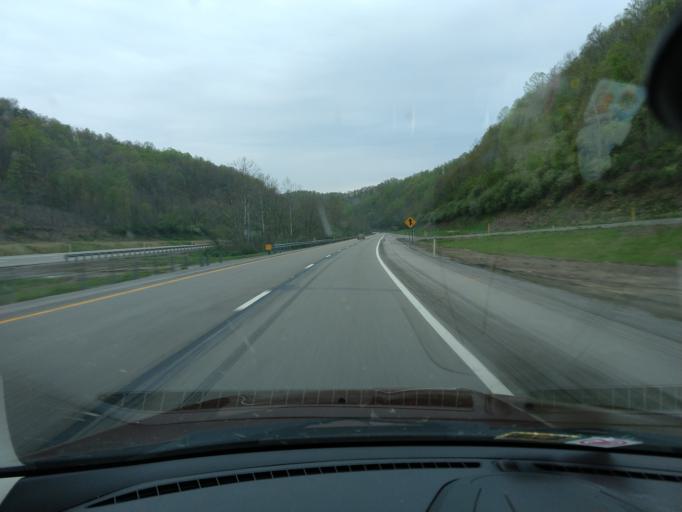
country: US
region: West Virginia
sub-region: Lewis County
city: Weston
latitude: 39.0140
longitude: -80.4675
